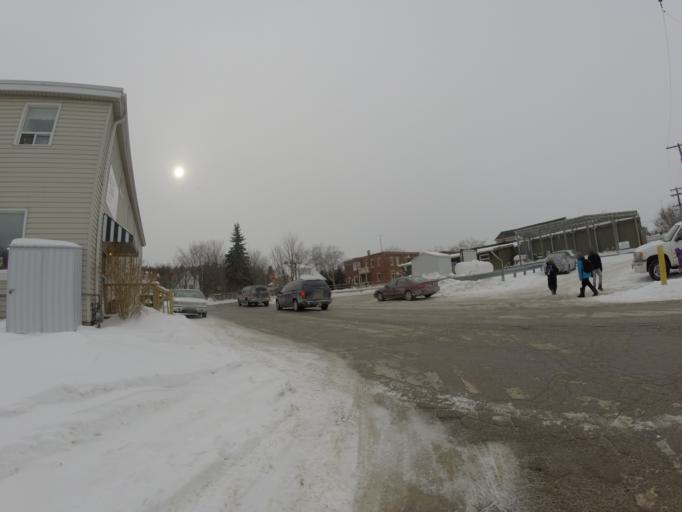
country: CA
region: Ontario
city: Orangeville
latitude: 43.7687
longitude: -80.0612
